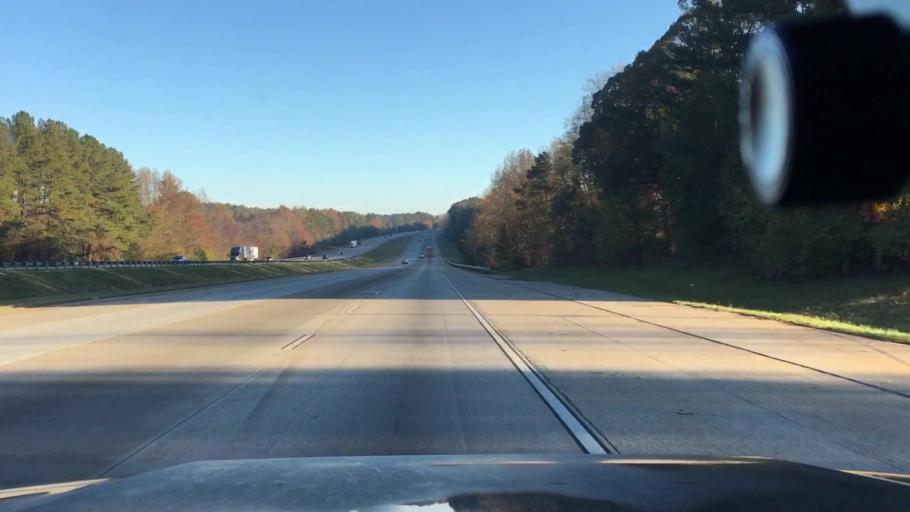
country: US
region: Georgia
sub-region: Fulton County
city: Palmetto
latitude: 33.4582
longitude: -84.6757
